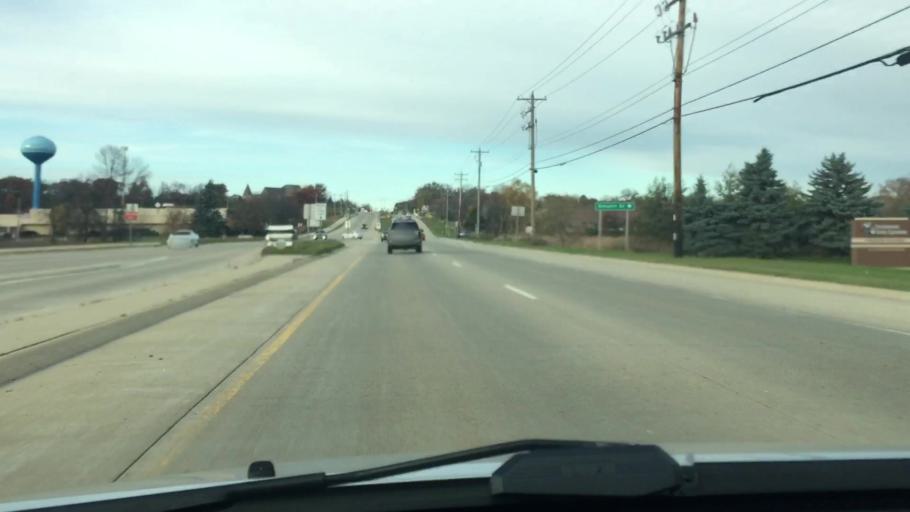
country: US
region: Wisconsin
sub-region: Waukesha County
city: Pewaukee
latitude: 43.0706
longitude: -88.2250
